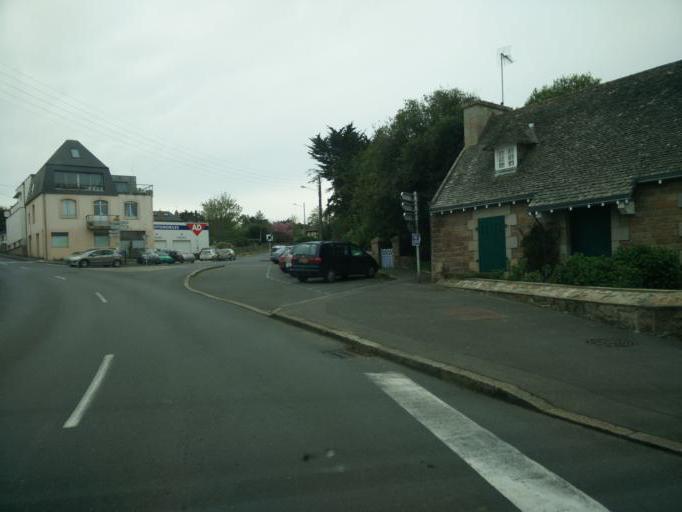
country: FR
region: Brittany
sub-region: Departement des Cotes-d'Armor
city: Trebeurden
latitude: 48.7713
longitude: -3.5779
